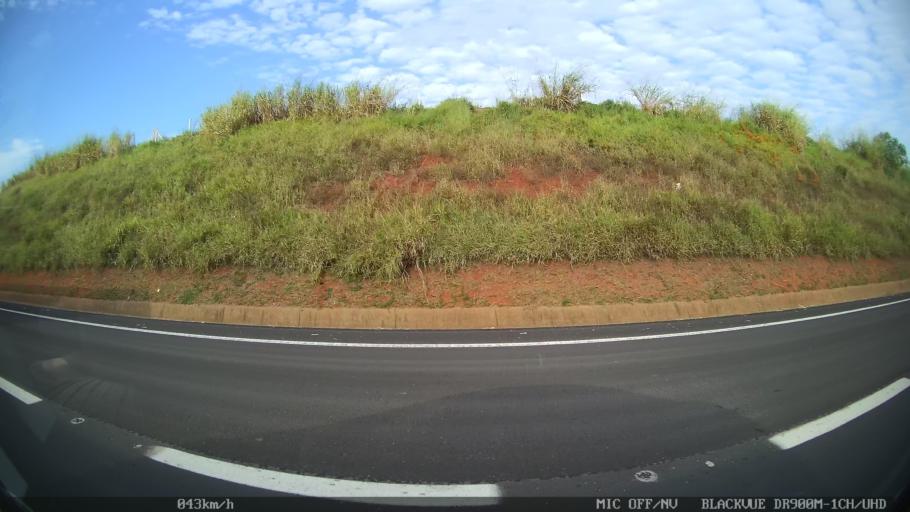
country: BR
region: Sao Paulo
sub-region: Cosmopolis
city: Cosmopolis
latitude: -22.6368
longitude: -47.2079
